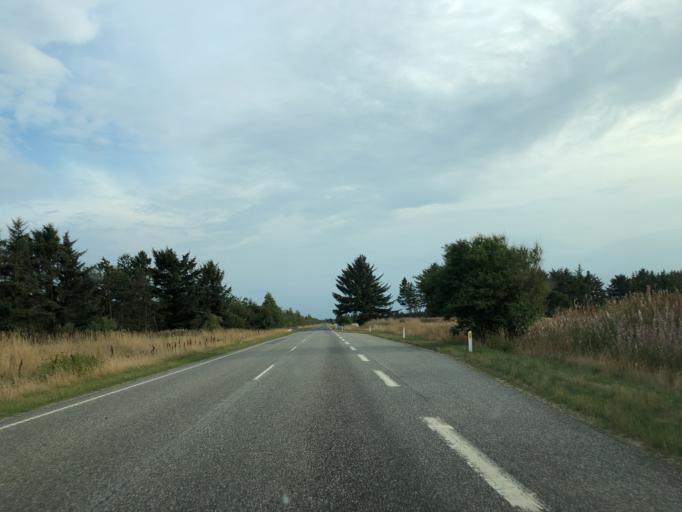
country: DK
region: Central Jutland
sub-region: Struer Kommune
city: Struer
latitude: 56.3948
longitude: 8.4585
